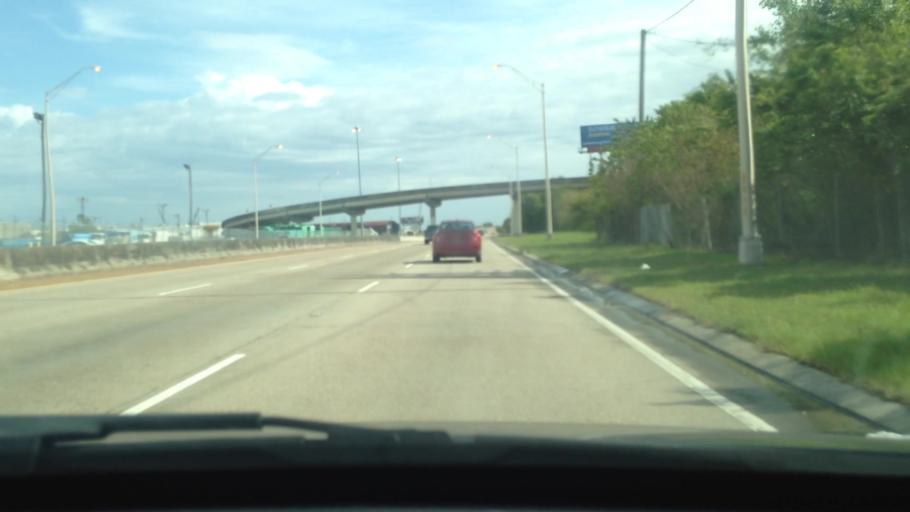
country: US
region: Louisiana
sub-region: Jefferson Parish
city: Jefferson
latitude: 29.9699
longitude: -90.1475
